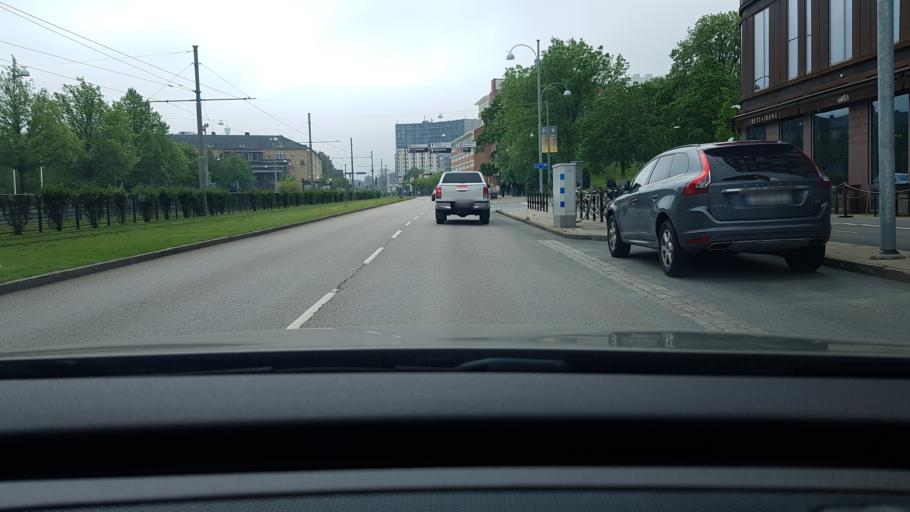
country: SE
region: Vaestra Goetaland
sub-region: Goteborg
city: Goeteborg
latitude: 57.7058
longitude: 11.9847
